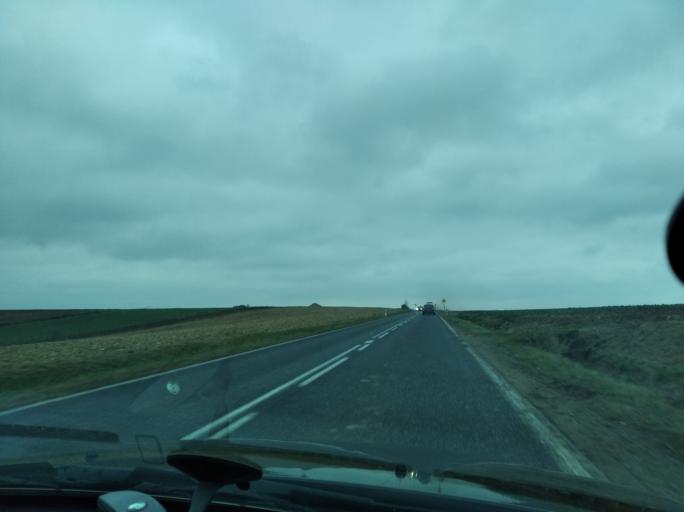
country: PL
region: Subcarpathian Voivodeship
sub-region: Powiat przeworski
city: Kanczuga
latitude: 49.9926
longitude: 22.3811
